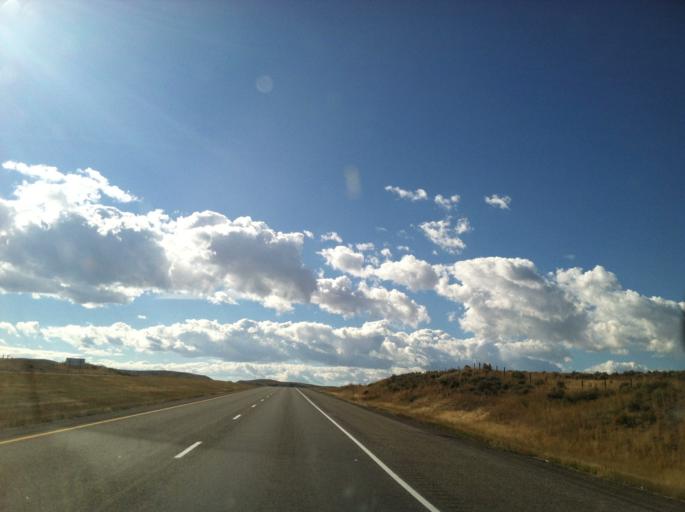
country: US
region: Montana
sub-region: Gallatin County
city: Three Forks
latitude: 45.9196
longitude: -111.6356
